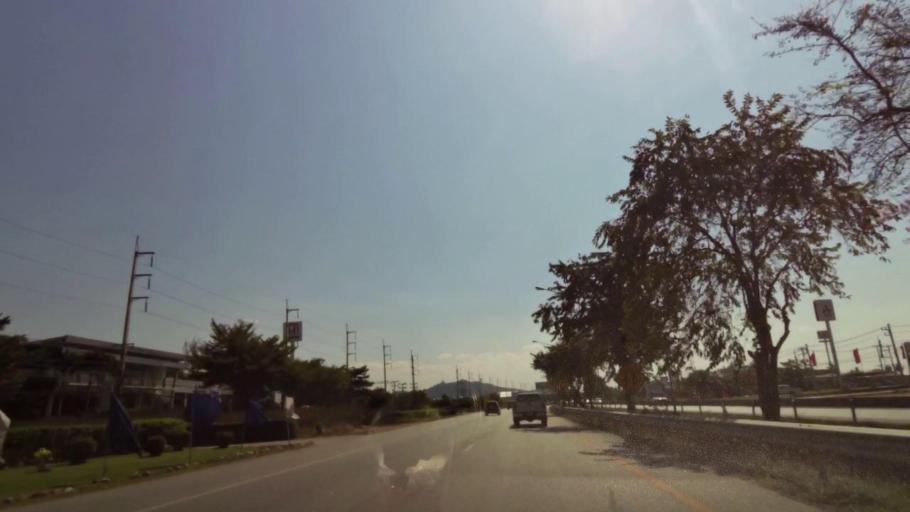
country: TH
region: Nakhon Sawan
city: Nakhon Sawan
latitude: 15.7483
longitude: 100.1227
